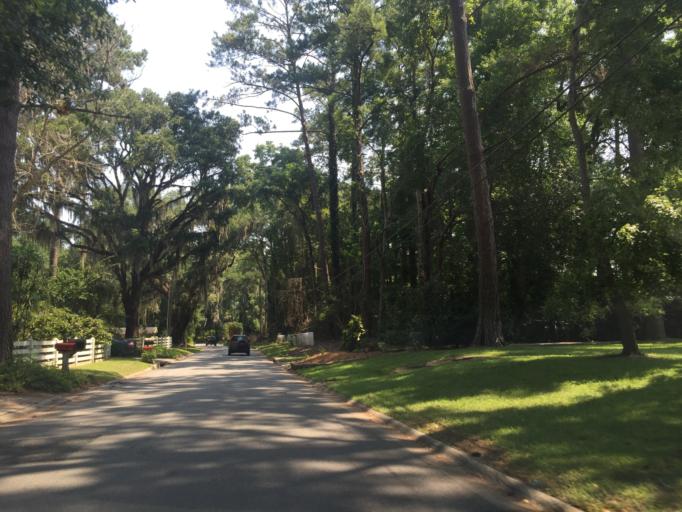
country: US
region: Georgia
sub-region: Chatham County
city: Montgomery
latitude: 31.9699
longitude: -81.1292
